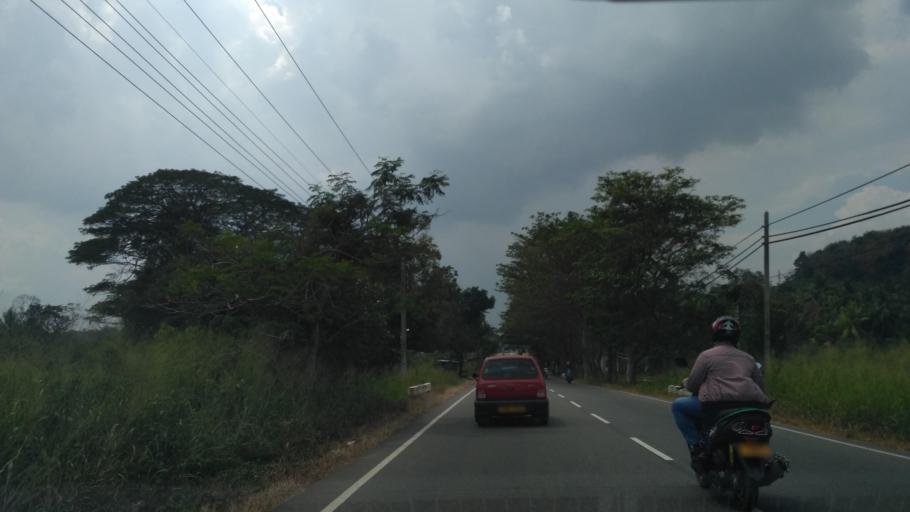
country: LK
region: North Western
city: Kuliyapitiya
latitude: 7.3251
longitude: 80.1094
